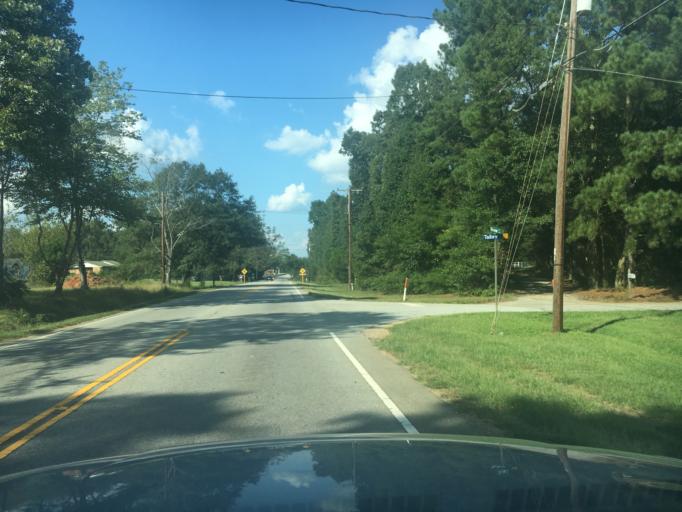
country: US
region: South Carolina
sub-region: Greenville County
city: Simpsonville
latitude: 34.6749
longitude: -82.2580
